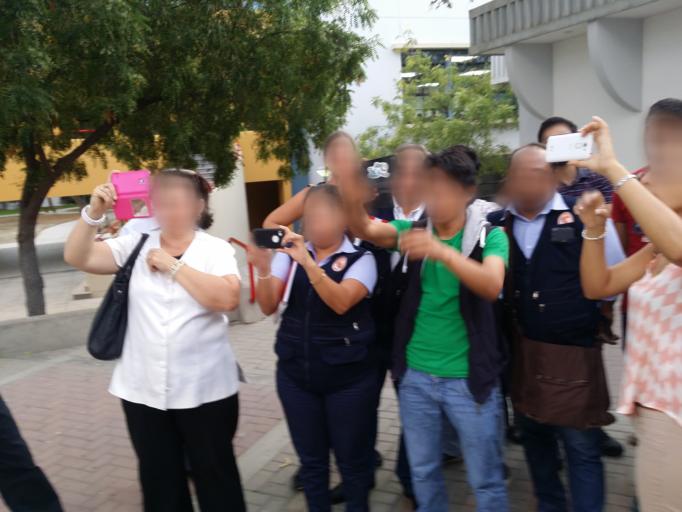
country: PE
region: Piura
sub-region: Provincia de Piura
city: Piura
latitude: -5.1757
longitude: -80.6351
